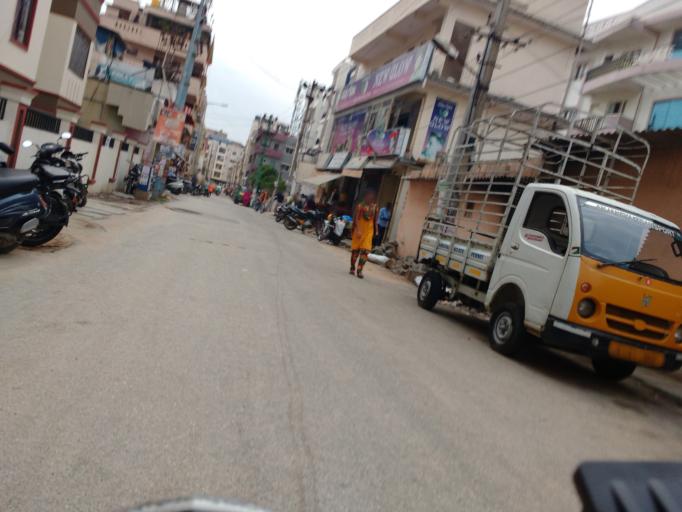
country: IN
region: Karnataka
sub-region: Bangalore Urban
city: Bangalore
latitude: 12.9909
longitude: 77.6706
